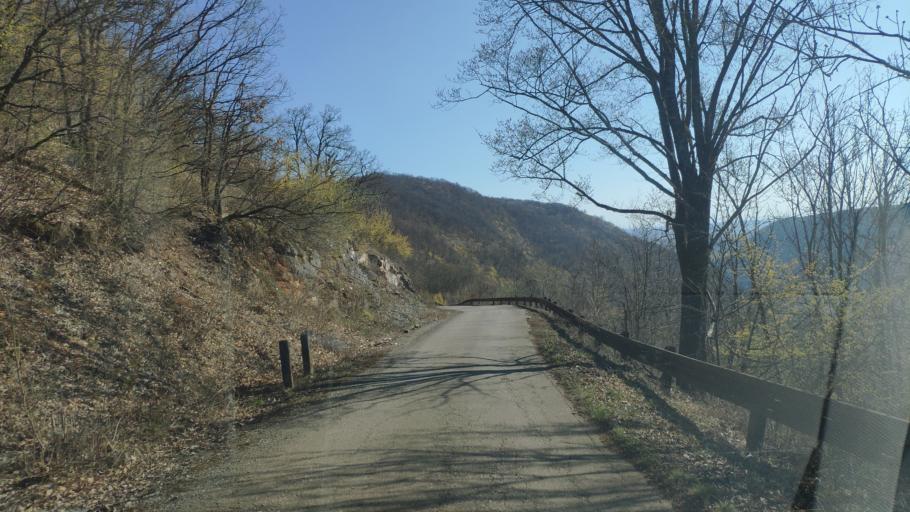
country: SK
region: Kosicky
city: Roznava
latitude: 48.5782
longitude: 20.4051
